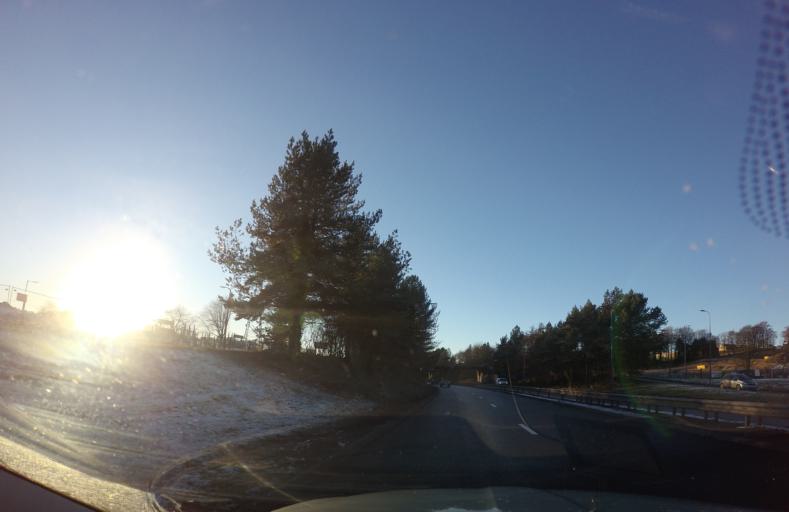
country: GB
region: Scotland
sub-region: Dundee City
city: Dundee
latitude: 56.4818
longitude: -3.0159
